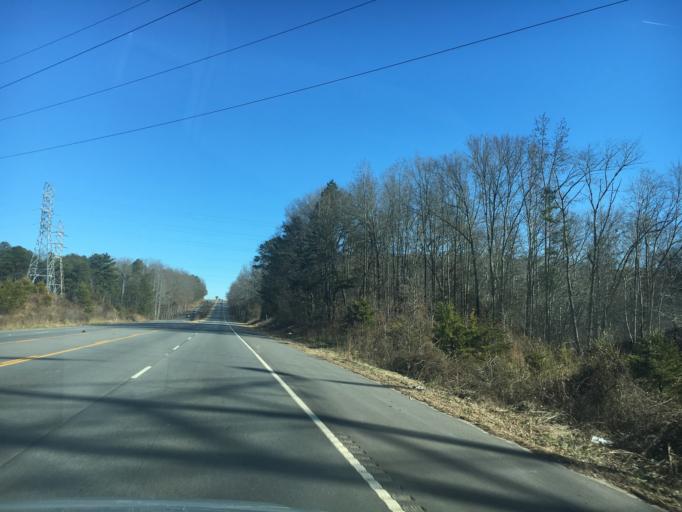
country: US
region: South Carolina
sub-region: Spartanburg County
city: Duncan
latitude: 34.9555
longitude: -82.1561
